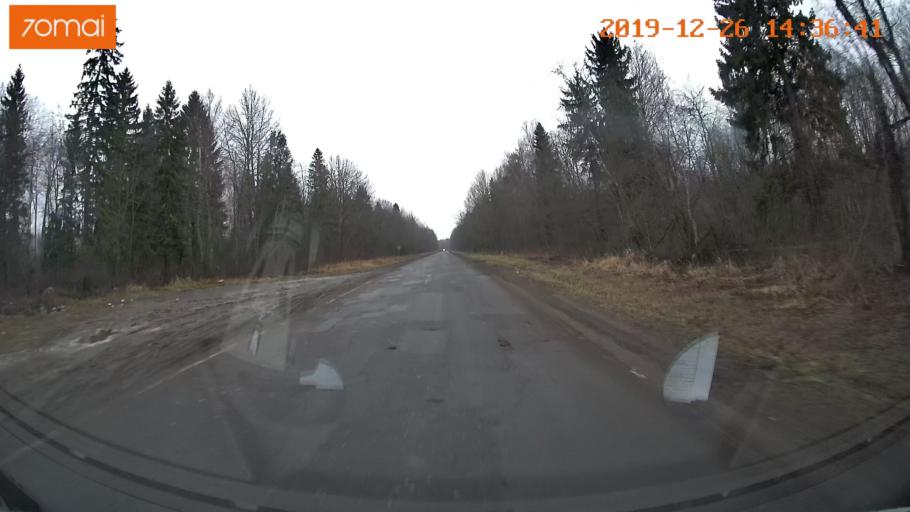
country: RU
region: Jaroslavl
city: Poshekhon'ye
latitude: 58.4091
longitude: 38.9751
